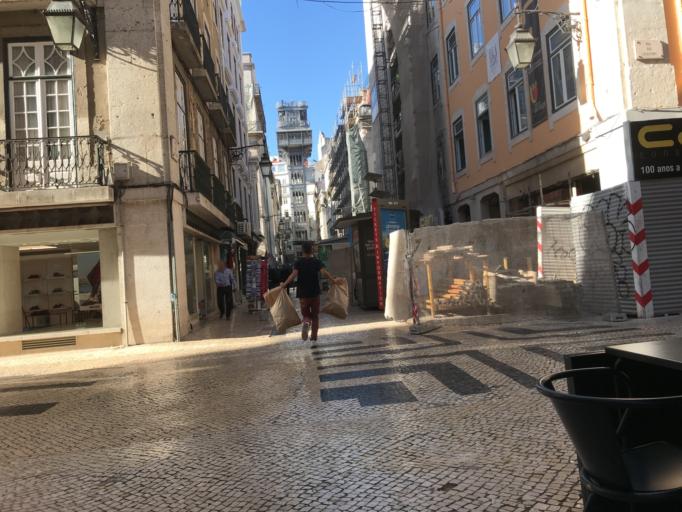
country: PT
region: Lisbon
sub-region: Lisbon
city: Lisbon
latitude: 38.7125
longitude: -9.1377
